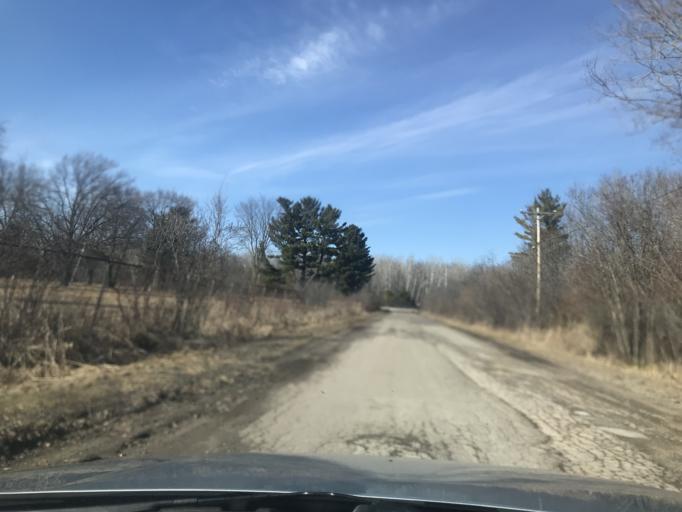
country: US
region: Wisconsin
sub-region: Marinette County
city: Marinette
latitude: 45.1136
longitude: -87.6509
